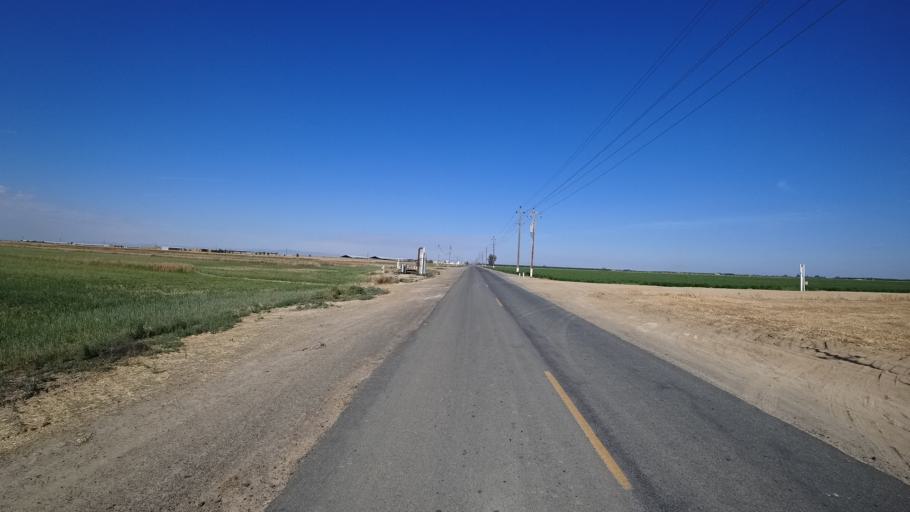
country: US
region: California
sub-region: Kings County
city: Home Garden
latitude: 36.2256
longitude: -119.6772
